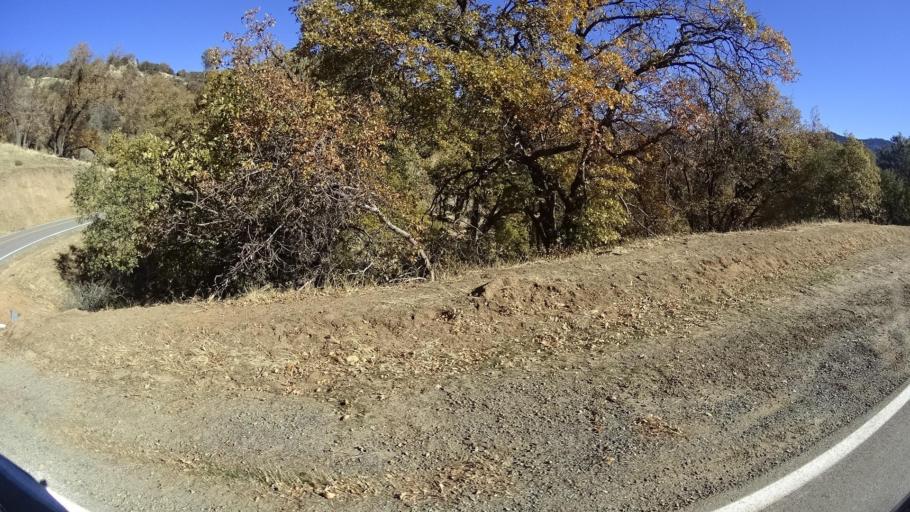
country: US
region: California
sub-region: Kern County
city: Alta Sierra
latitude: 35.7401
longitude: -118.6094
